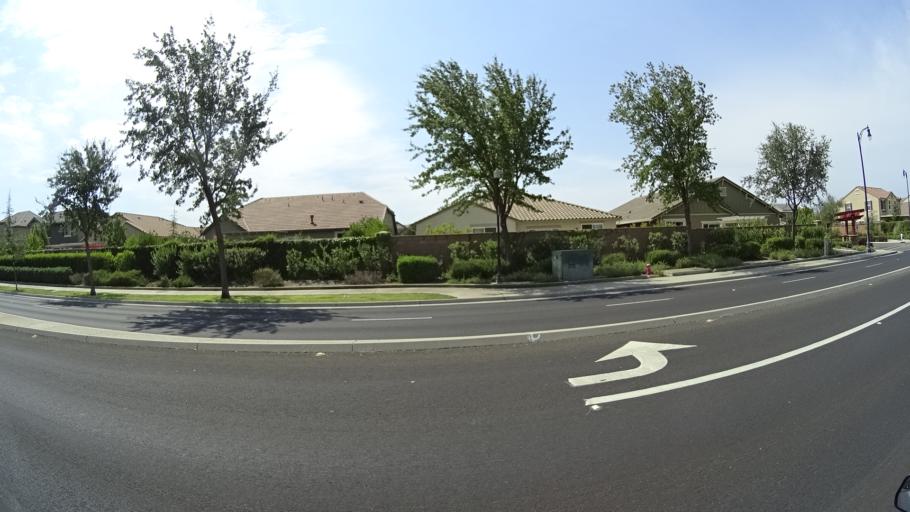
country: US
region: California
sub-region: Sacramento County
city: Laguna
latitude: 38.3943
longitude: -121.4108
